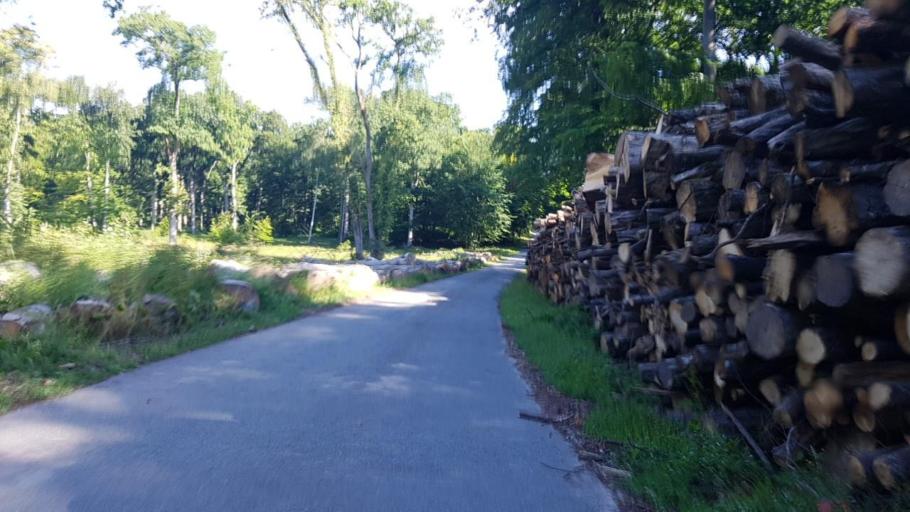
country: FR
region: Picardie
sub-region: Departement de l'Oise
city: Fleurines
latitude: 49.2654
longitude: 2.6177
